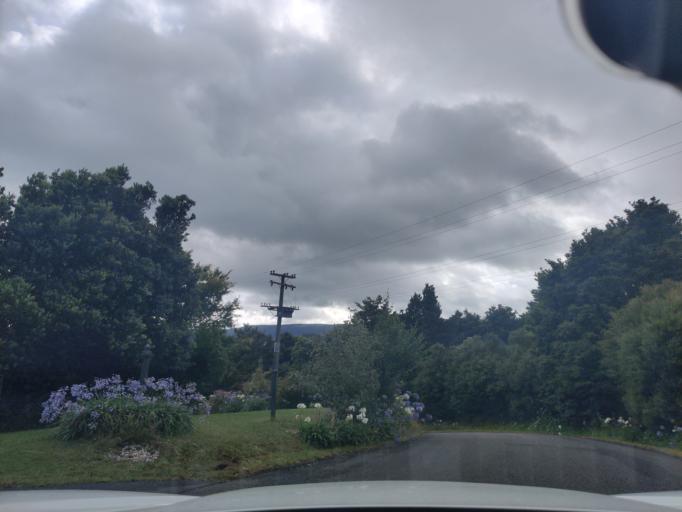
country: NZ
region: Manawatu-Wanganui
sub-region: Palmerston North City
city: Palmerston North
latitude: -40.3774
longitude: 175.6644
